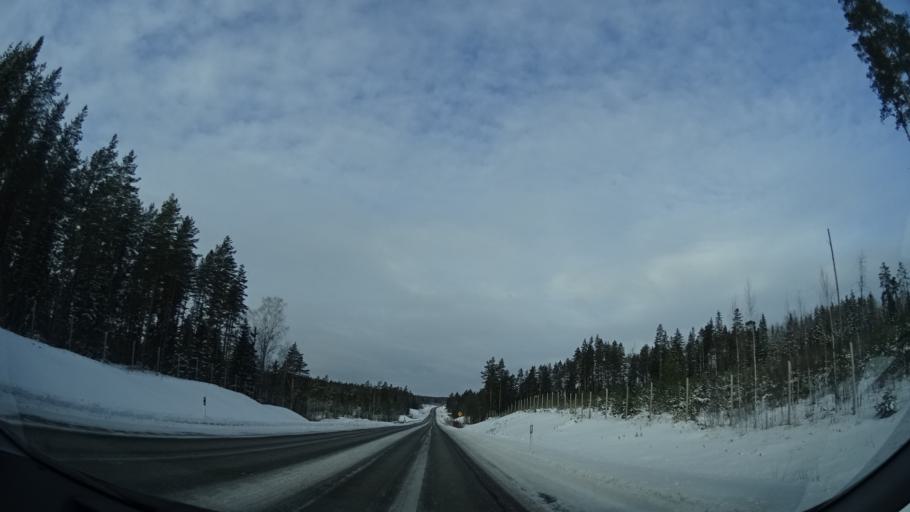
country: FI
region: Uusimaa
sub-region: Helsinki
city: Karkkila
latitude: 60.5890
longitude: 24.1156
